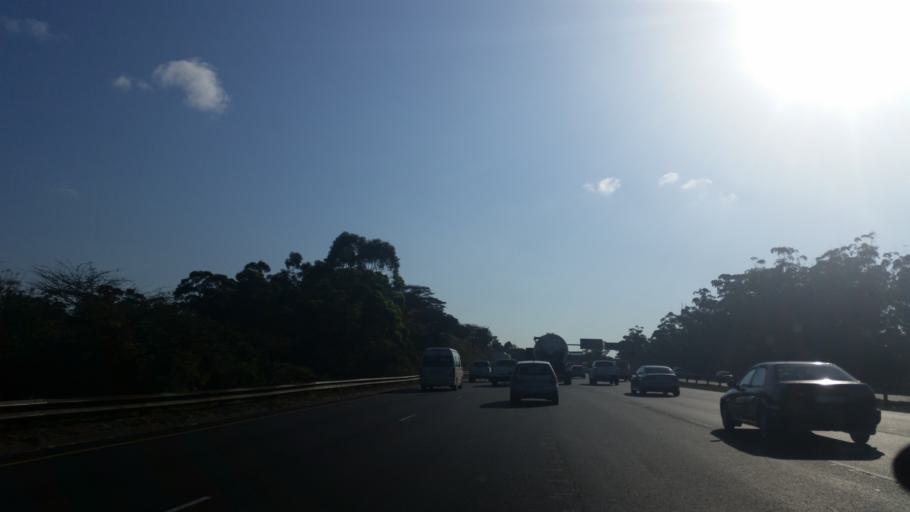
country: ZA
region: KwaZulu-Natal
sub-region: eThekwini Metropolitan Municipality
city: Berea
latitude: -29.8352
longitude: 30.9592
